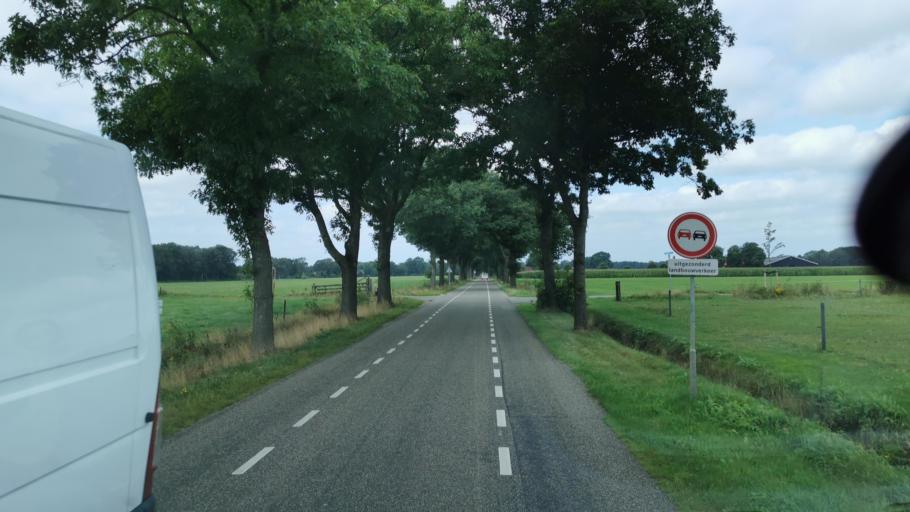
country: NL
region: Overijssel
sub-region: Gemeente Oldenzaal
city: Oldenzaal
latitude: 52.3194
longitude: 6.8775
